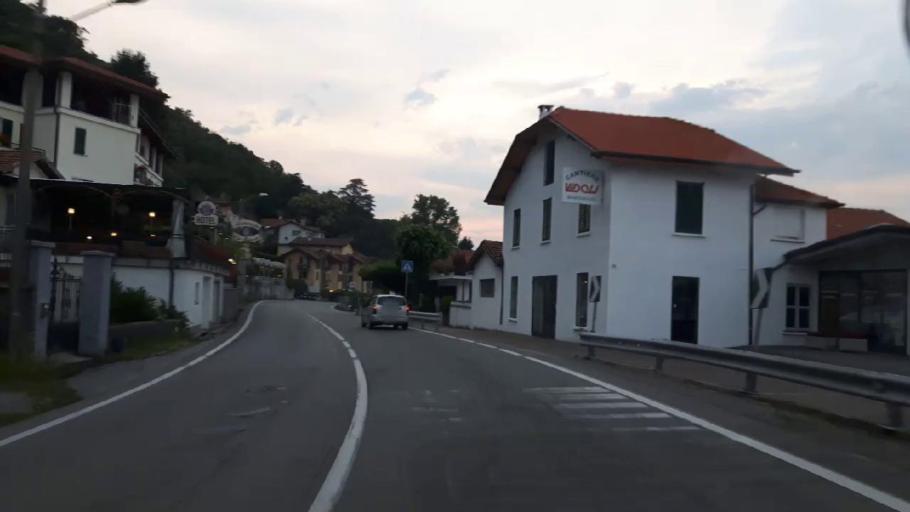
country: IT
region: Piedmont
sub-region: Provincia Verbano-Cusio-Ossola
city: Stresa
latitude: 45.8709
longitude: 8.5642
